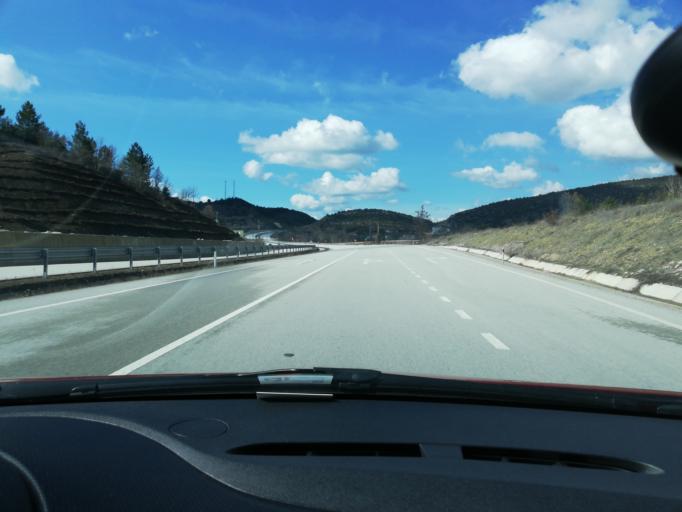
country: TR
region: Kastamonu
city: Igdir
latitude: 41.2313
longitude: 33.0378
